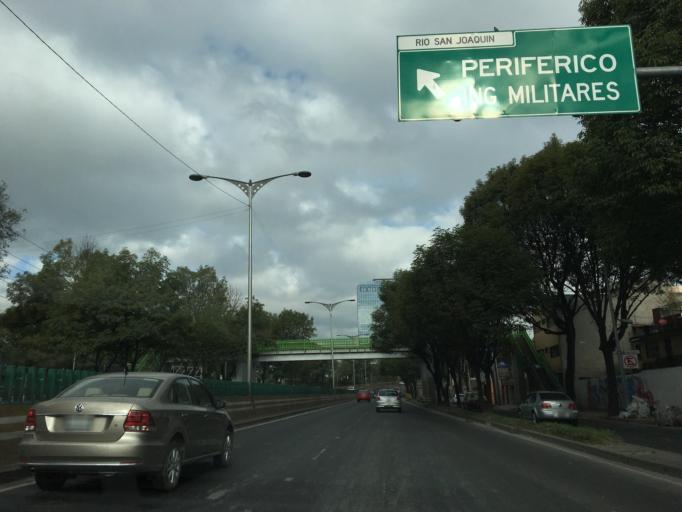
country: MX
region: Mexico City
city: Miguel Hidalgo
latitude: 19.4463
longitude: -99.2036
